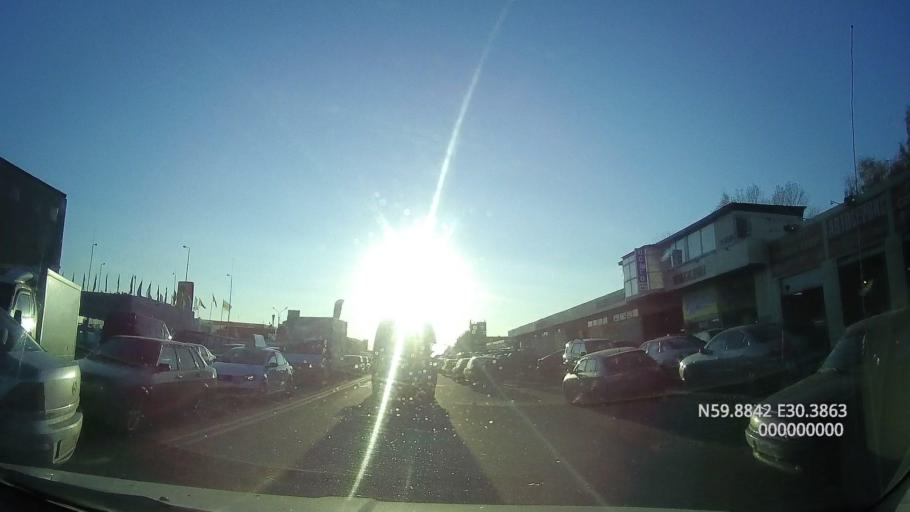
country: RU
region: St.-Petersburg
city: Kupchino
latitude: 59.8842
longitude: 30.3862
